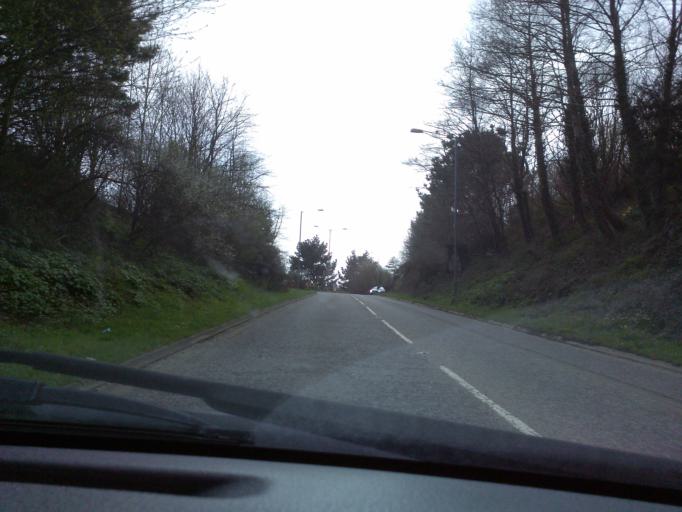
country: GB
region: England
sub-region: Cornwall
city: Penzance
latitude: 50.1152
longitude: -5.5566
